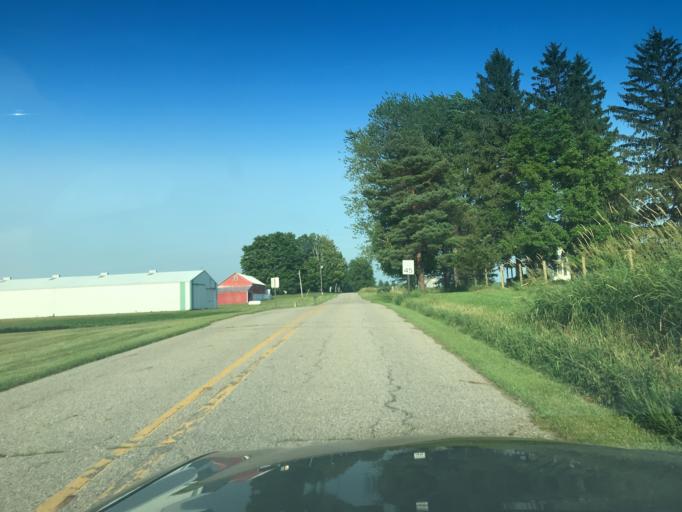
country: US
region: Michigan
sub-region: Ingham County
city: Mason
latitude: 42.5531
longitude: -84.4759
